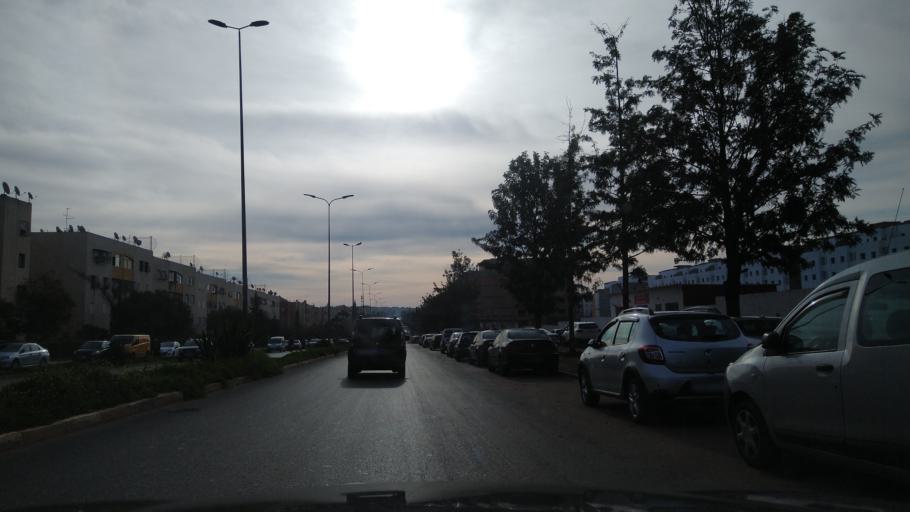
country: MA
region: Rabat-Sale-Zemmour-Zaer
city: Sale
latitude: 33.9973
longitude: -6.7477
